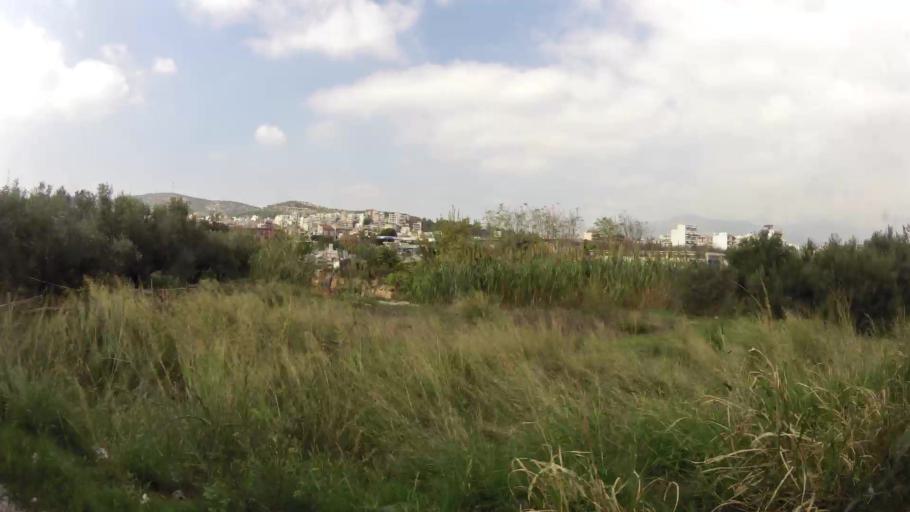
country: GR
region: Attica
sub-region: Nomarchia Dytikis Attikis
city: Zefyri
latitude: 38.0597
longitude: 23.7188
